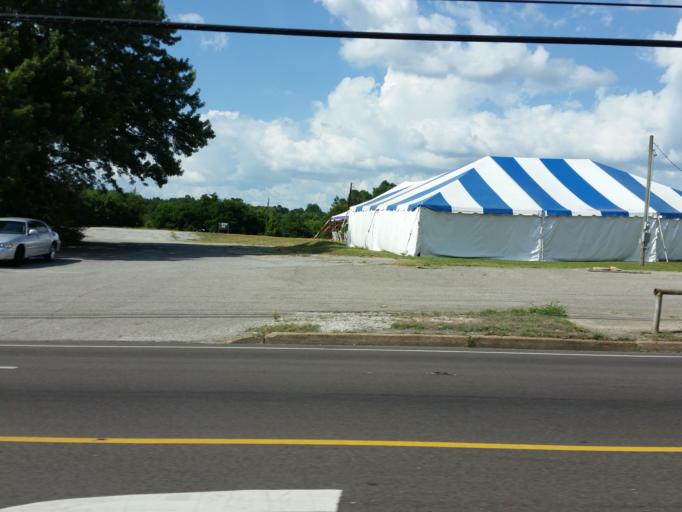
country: US
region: Tennessee
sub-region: Henderson County
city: Lexington
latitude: 35.6563
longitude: -88.4072
